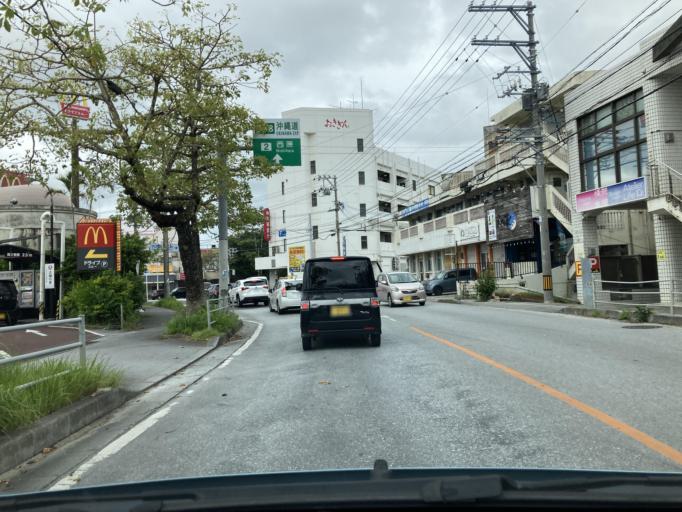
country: JP
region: Okinawa
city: Ginowan
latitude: 26.2382
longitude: 127.7495
